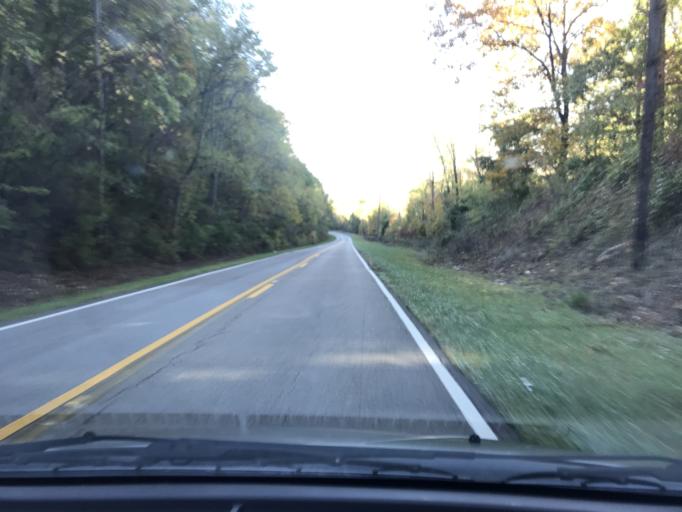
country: US
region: Georgia
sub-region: Dade County
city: Trenton
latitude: 34.8894
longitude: -85.4600
